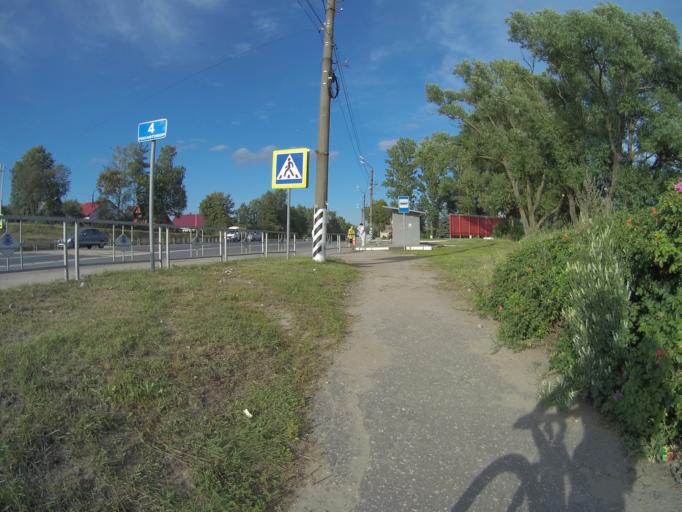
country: RU
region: Vladimir
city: Raduzhnyy
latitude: 56.0961
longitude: 40.2561
